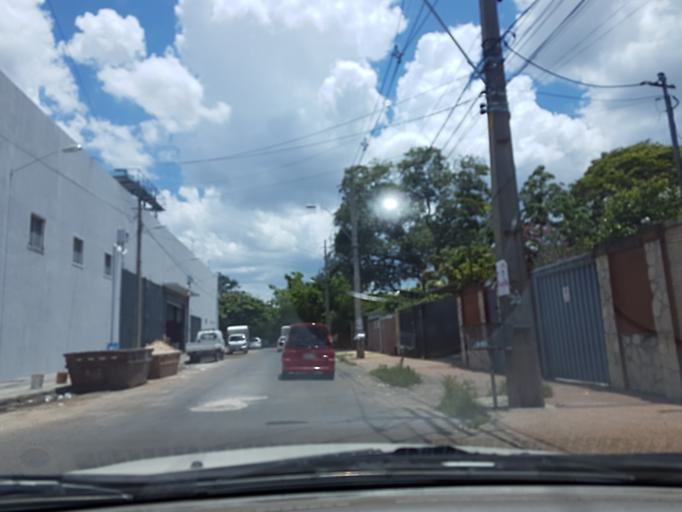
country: PY
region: Asuncion
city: Asuncion
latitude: -25.2719
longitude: -57.5855
